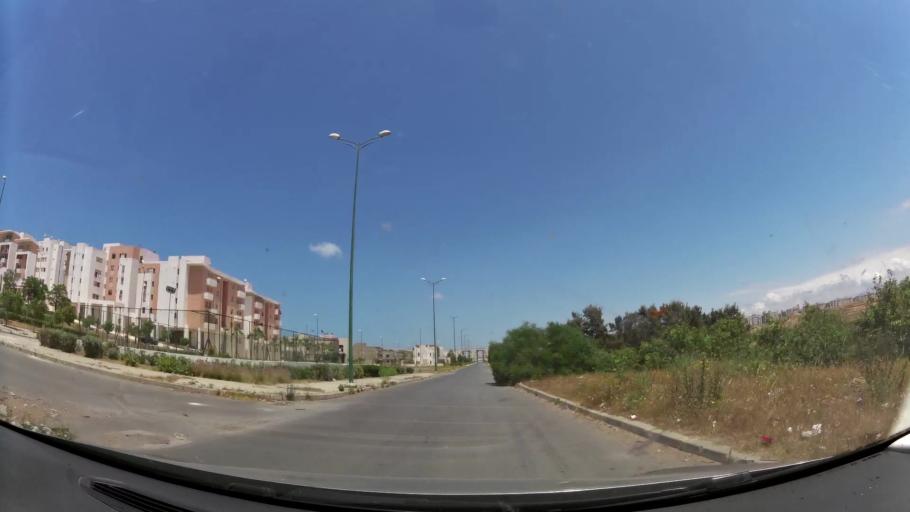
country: MA
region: Gharb-Chrarda-Beni Hssen
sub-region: Kenitra Province
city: Kenitra
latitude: 34.2494
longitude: -6.6497
